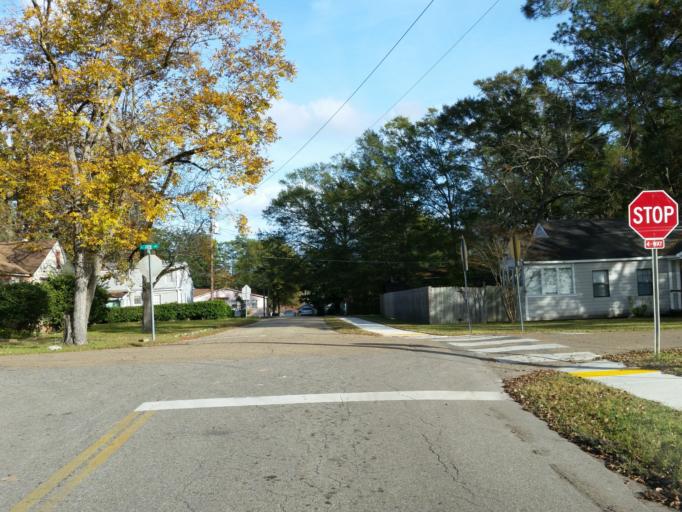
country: US
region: Mississippi
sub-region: Forrest County
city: Hattiesburg
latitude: 31.3229
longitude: -89.3208
